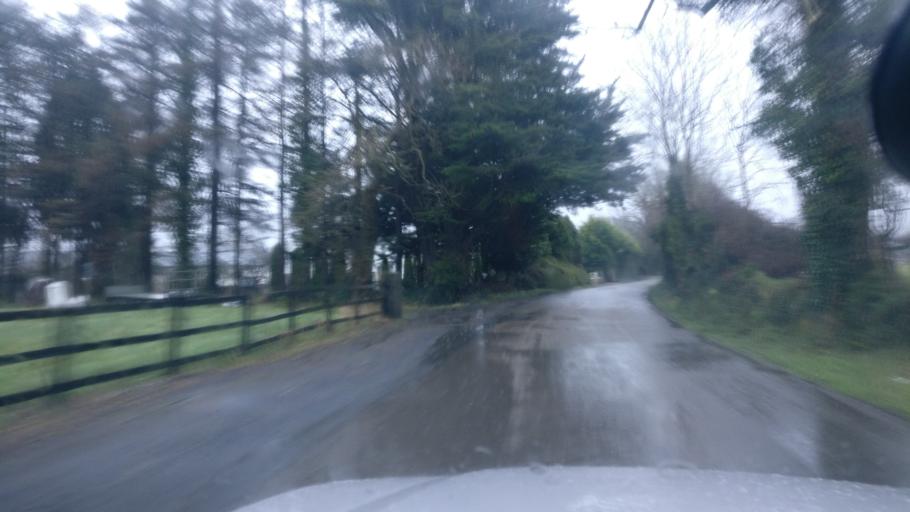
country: IE
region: Connaught
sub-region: County Galway
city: Ballinasloe
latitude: 53.3077
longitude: -8.3434
